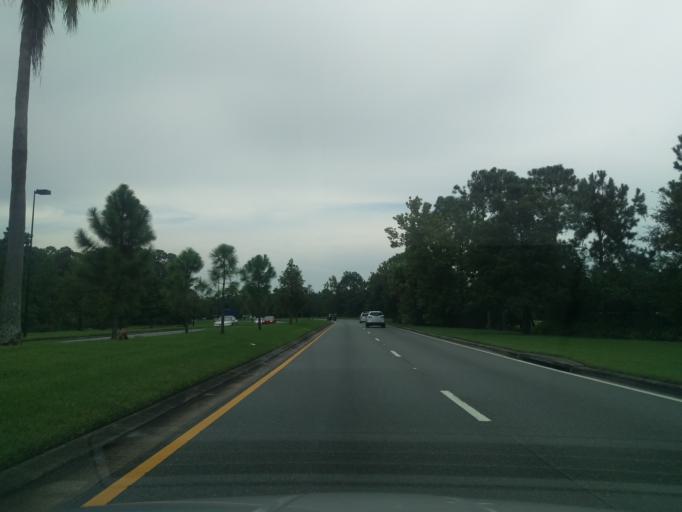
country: US
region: Florida
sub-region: Osceola County
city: Celebration
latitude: 28.3795
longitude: -81.5386
